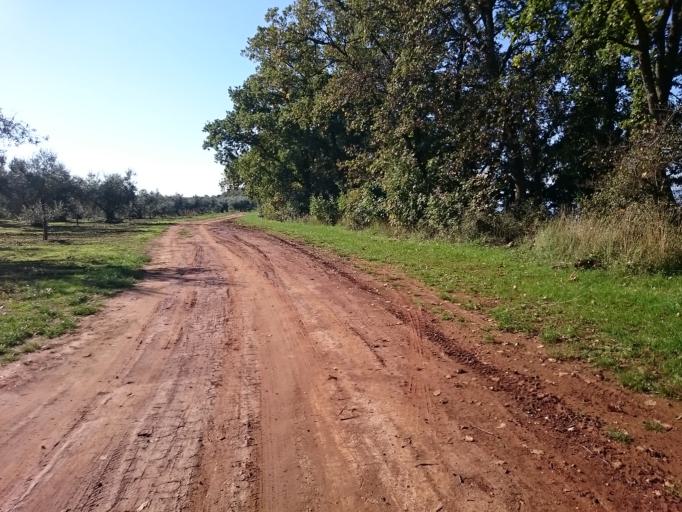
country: HR
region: Istarska
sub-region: Grad Porec
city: Porec
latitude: 45.2729
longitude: 13.5830
